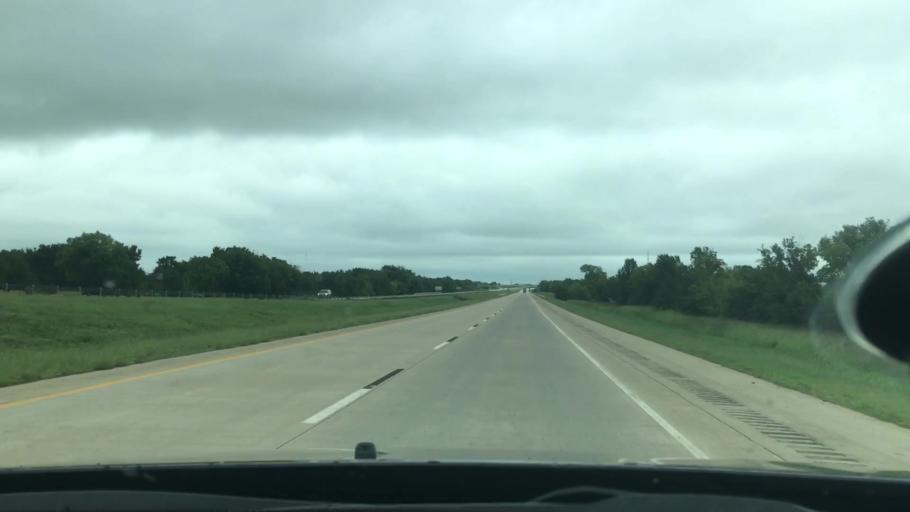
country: US
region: Oklahoma
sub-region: McIntosh County
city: Checotah
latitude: 35.4573
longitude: -95.5697
